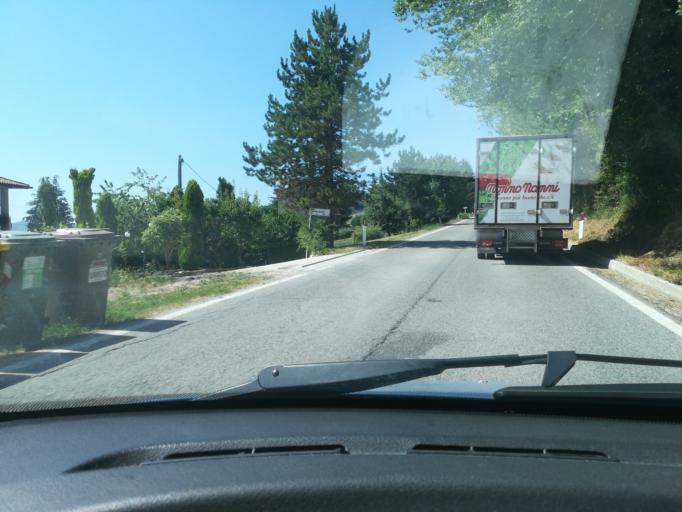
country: IT
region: The Marches
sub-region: Provincia di Macerata
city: San Ginesio
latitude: 43.1090
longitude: 13.3384
